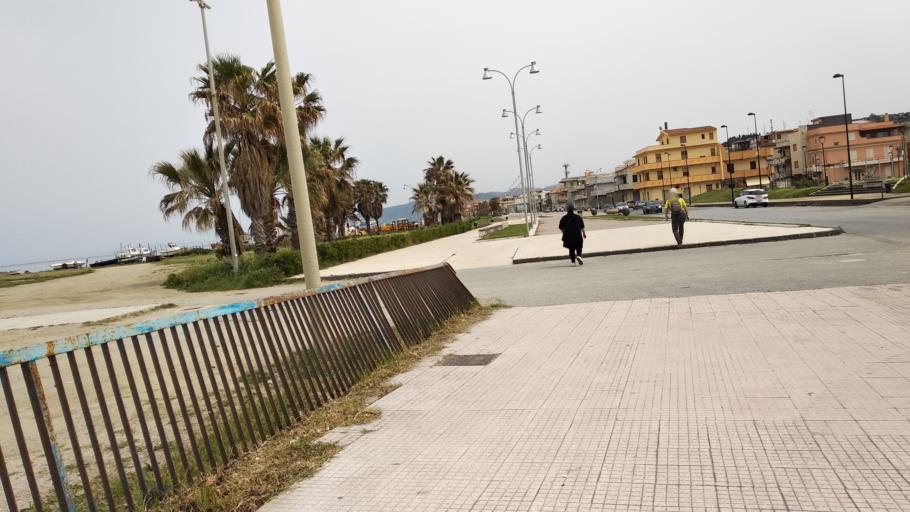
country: IT
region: Sicily
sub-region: Messina
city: Venetico Marina
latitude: 38.2230
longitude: 15.3733
